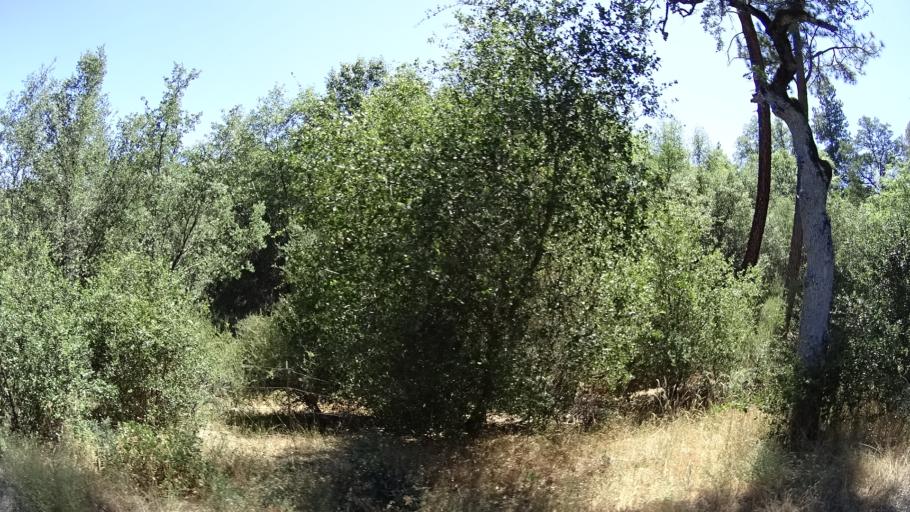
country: US
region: California
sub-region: Calaveras County
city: Mountain Ranch
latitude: 38.2993
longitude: -120.4875
